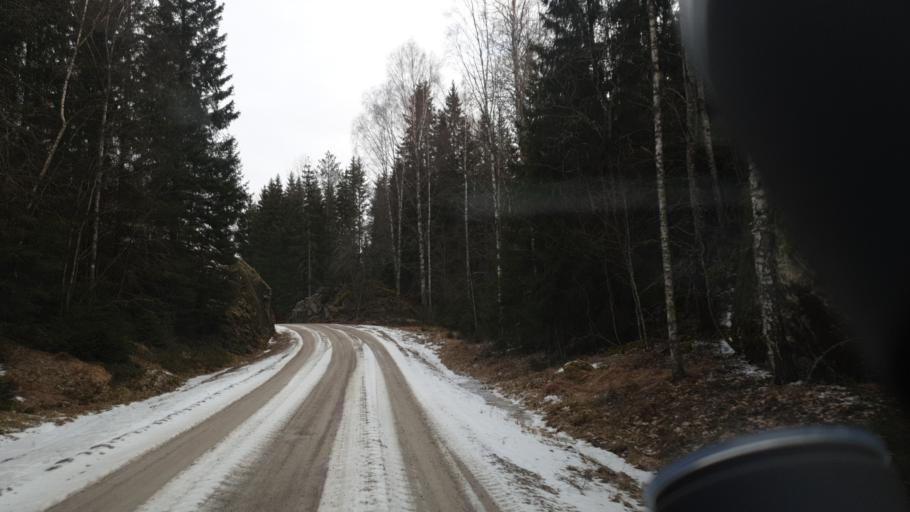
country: SE
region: Vaermland
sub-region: Eda Kommun
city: Amotfors
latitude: 59.7960
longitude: 12.4454
